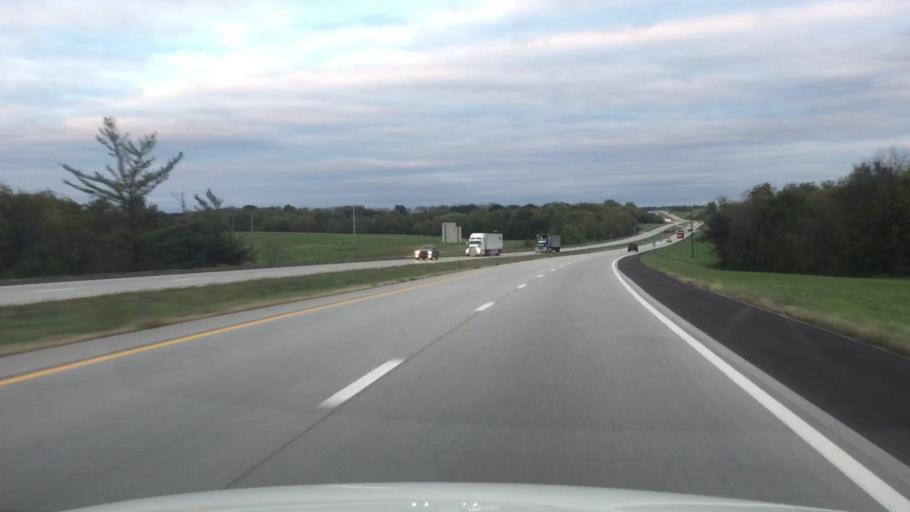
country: US
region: Missouri
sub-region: Lafayette County
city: Concordia
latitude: 38.9916
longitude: -93.6521
